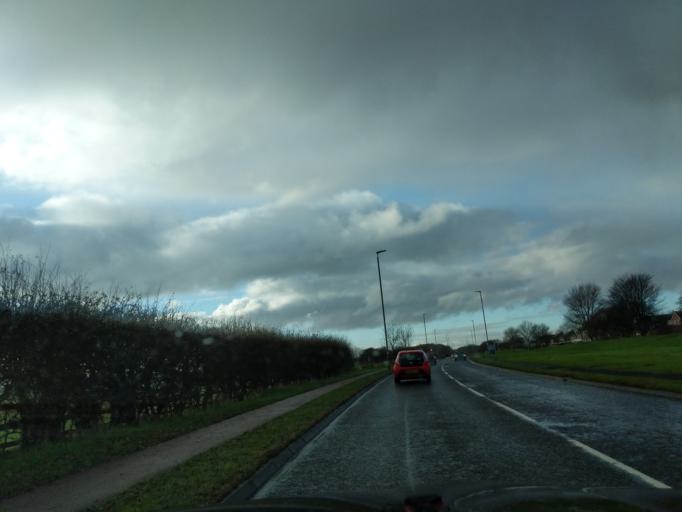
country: GB
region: England
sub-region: Northumberland
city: Blyth
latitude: 55.1079
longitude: -1.5058
